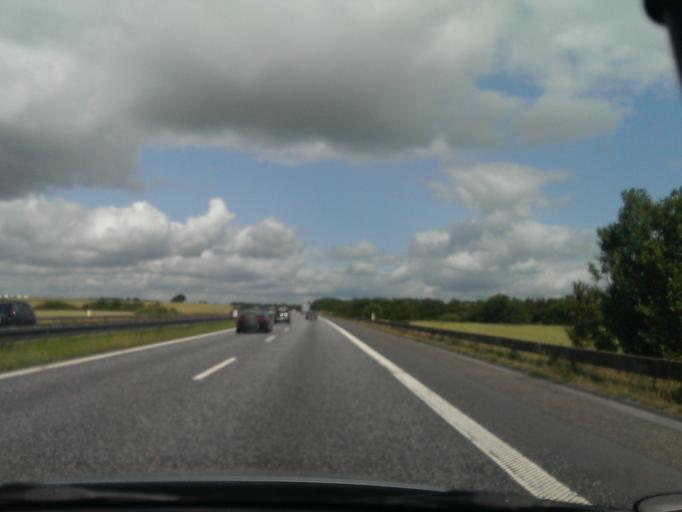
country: DK
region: Central Jutland
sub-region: Randers Kommune
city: Spentrup
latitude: 56.5170
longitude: 9.9616
